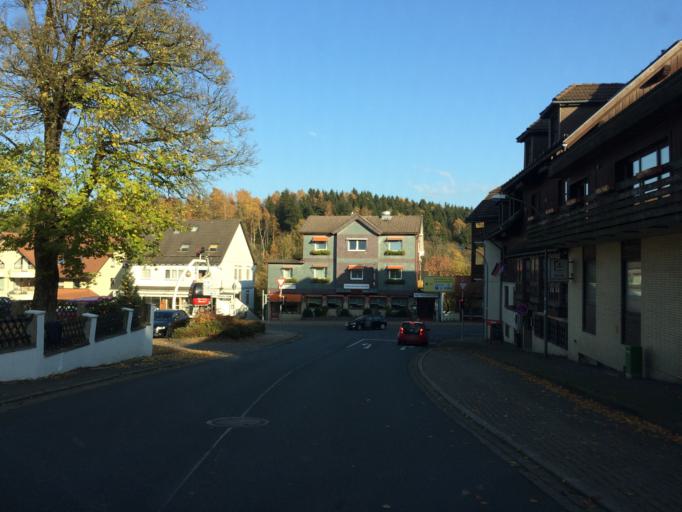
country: DE
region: Lower Saxony
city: Braunlage
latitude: 51.7225
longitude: 10.6111
